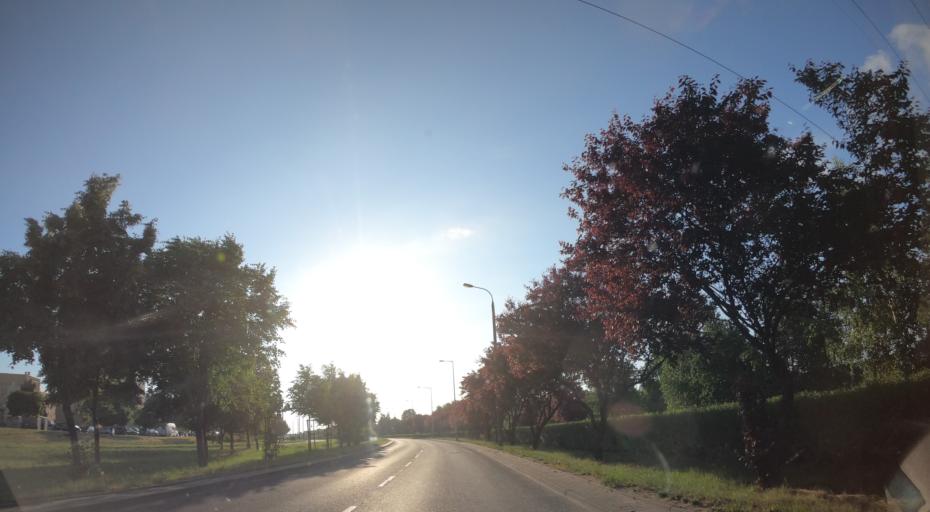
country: PL
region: Lubusz
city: Gorzow Wielkopolski
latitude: 52.7579
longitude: 15.2654
